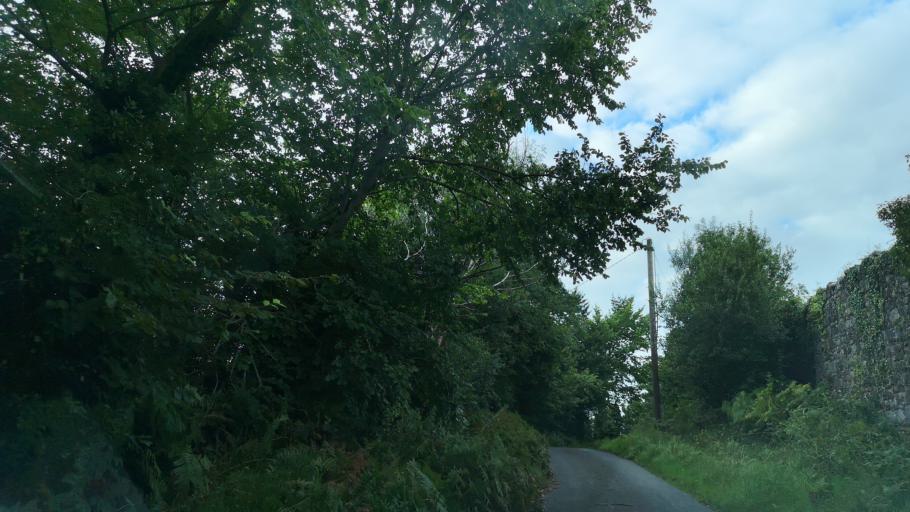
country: IE
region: Connaught
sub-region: County Galway
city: Loughrea
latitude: 53.1483
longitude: -8.4982
